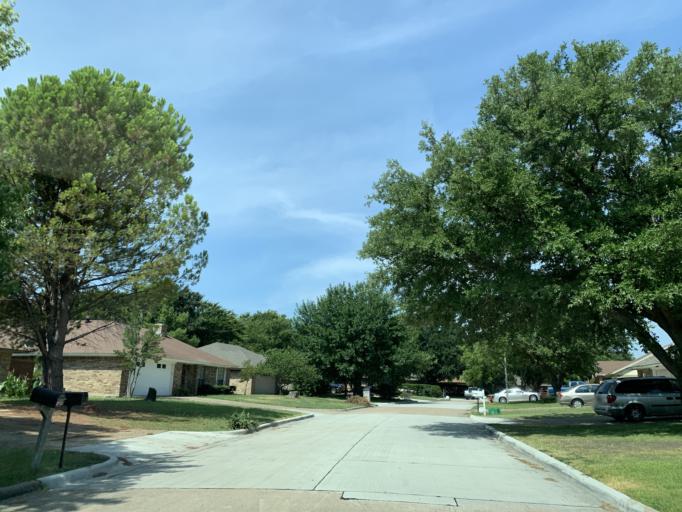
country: US
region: Texas
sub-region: Dallas County
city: Grand Prairie
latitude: 32.6683
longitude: -97.0386
